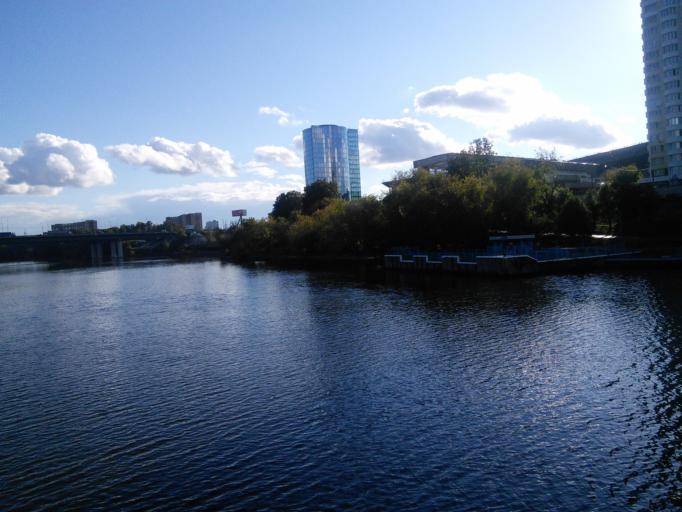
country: RU
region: Moskovskaya
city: Levoberezhnaya
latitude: 55.8870
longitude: 37.4599
